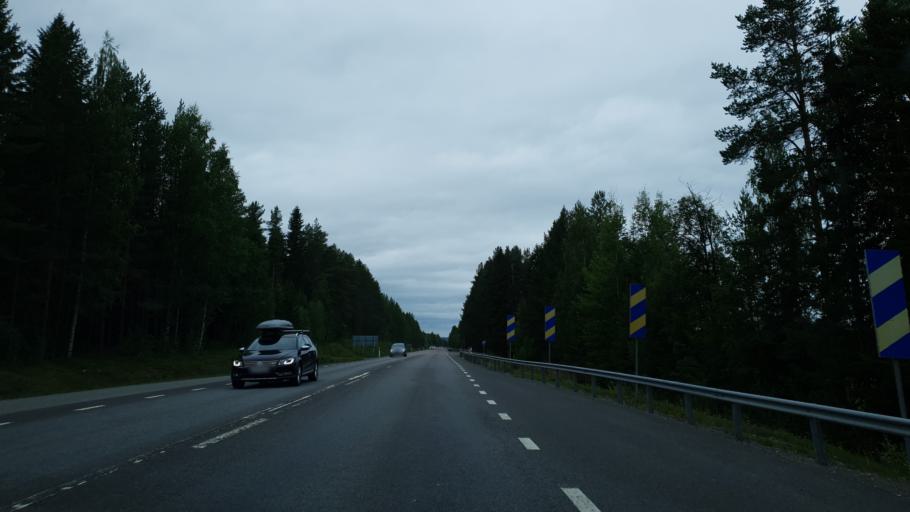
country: SE
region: Vaesterbotten
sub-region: Skelleftea Kommun
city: Viken
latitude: 64.7648
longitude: 20.8718
